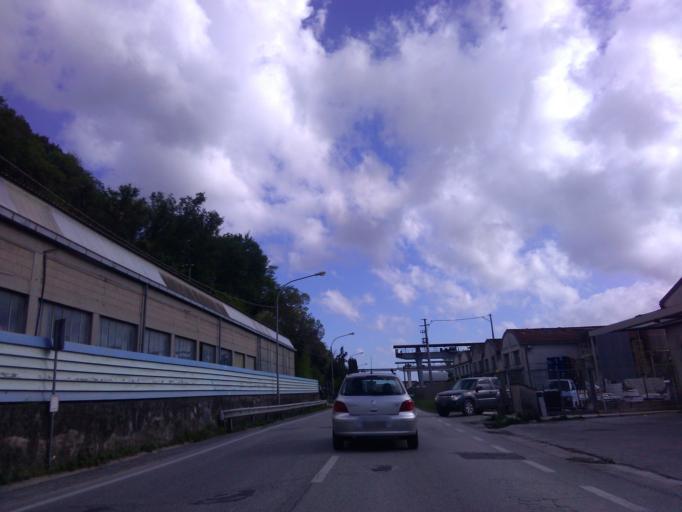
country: IT
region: Tuscany
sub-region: Provincia di Lucca
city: Ripa-Pozzi-Querceta-Ponterosso
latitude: 43.9751
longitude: 10.2202
